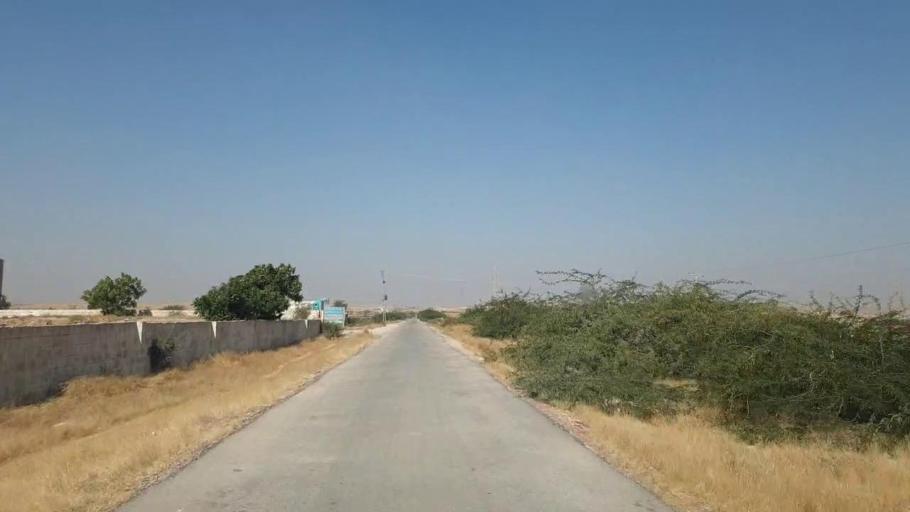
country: PK
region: Sindh
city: Thatta
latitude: 25.1838
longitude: 67.8054
